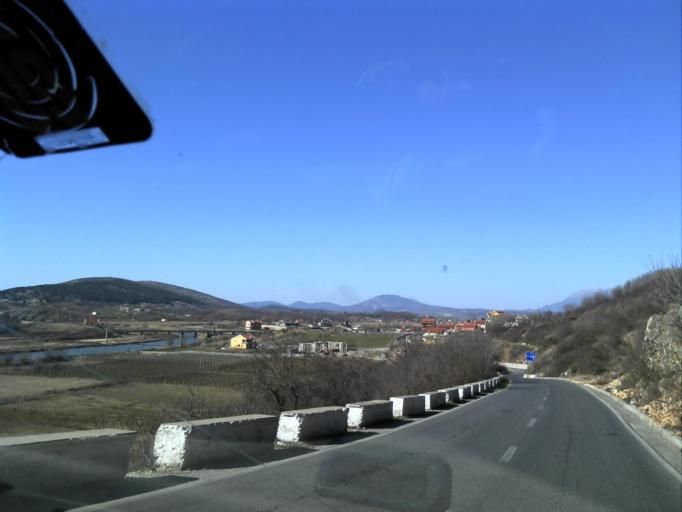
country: AL
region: Shkoder
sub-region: Rrethi i Shkodres
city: Velipoje
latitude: 41.9158
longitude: 19.4271
